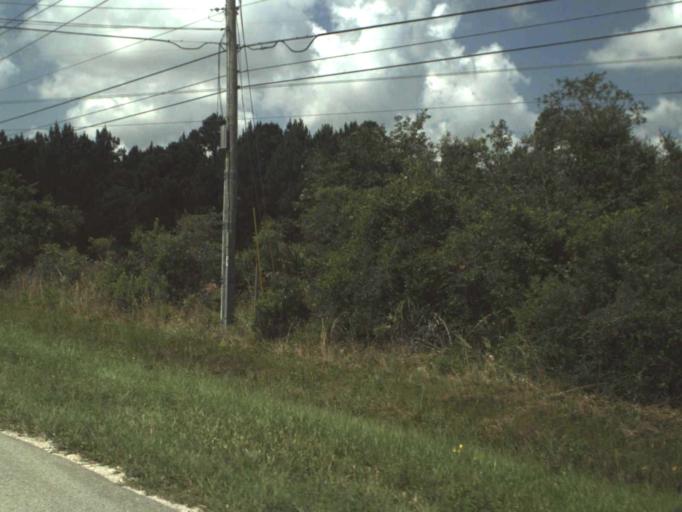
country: US
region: Florida
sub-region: Volusia County
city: Samsula-Spruce Creek
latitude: 28.9898
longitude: -81.0723
